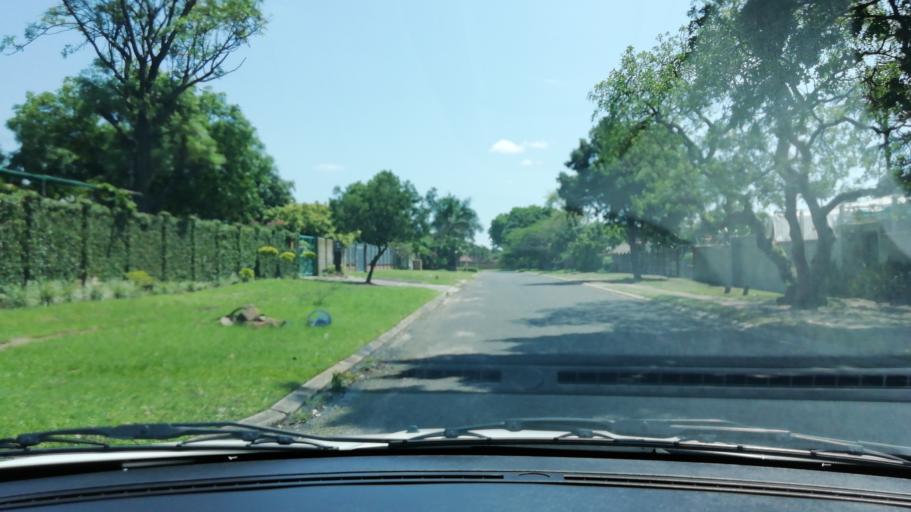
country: ZA
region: KwaZulu-Natal
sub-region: uThungulu District Municipality
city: Richards Bay
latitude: -28.7401
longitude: 32.0592
